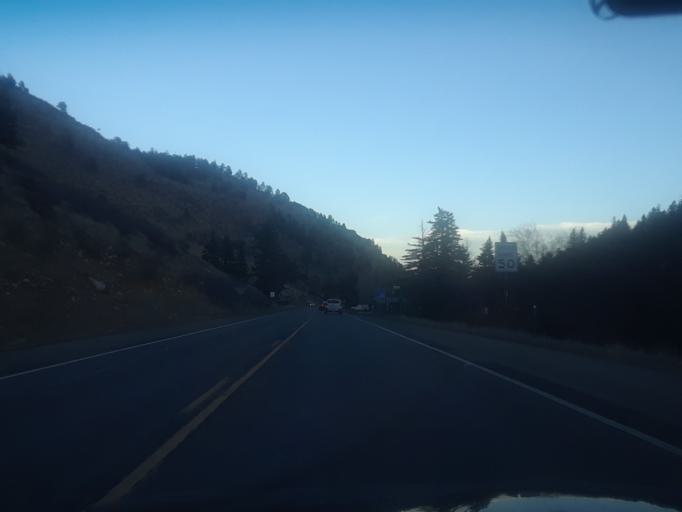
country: US
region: Colorado
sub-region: Clear Creek County
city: Georgetown
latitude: 39.4602
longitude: -105.6673
